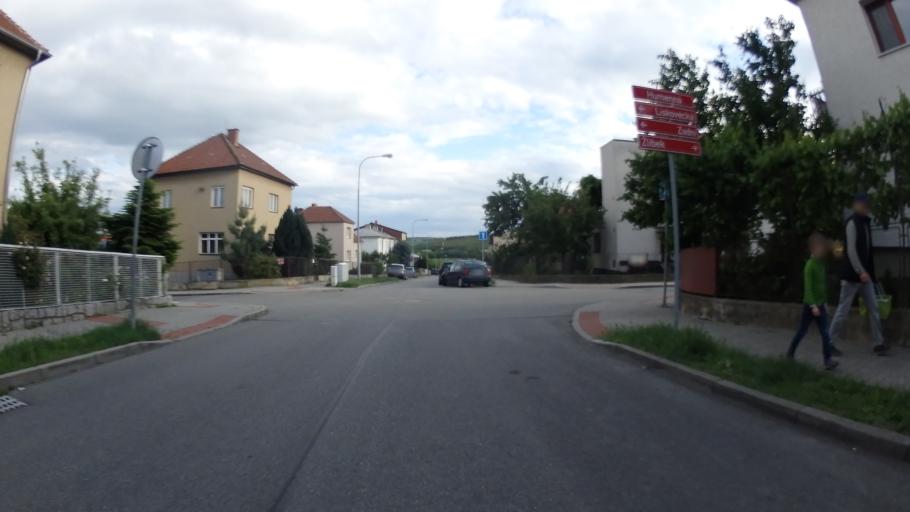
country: CZ
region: South Moravian
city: Moravany
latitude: 49.1667
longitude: 16.5733
